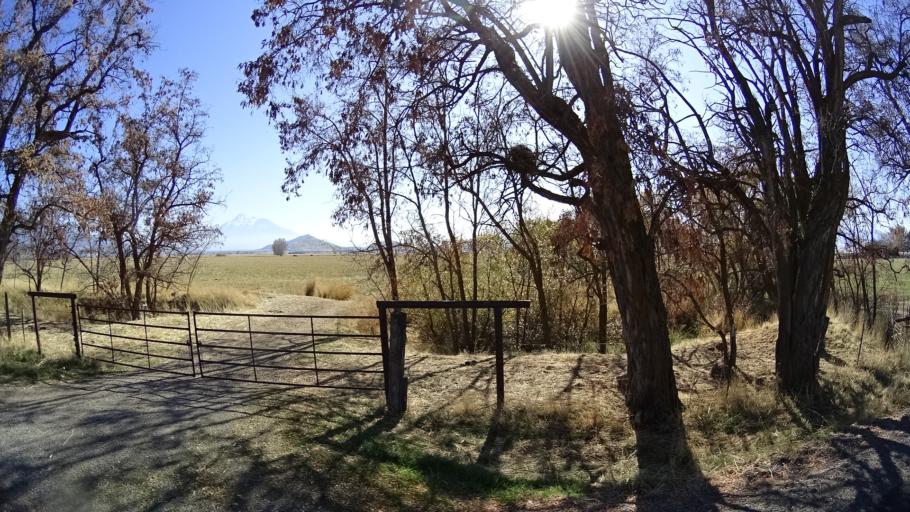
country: US
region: California
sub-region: Siskiyou County
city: Montague
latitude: 41.7262
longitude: -122.4122
